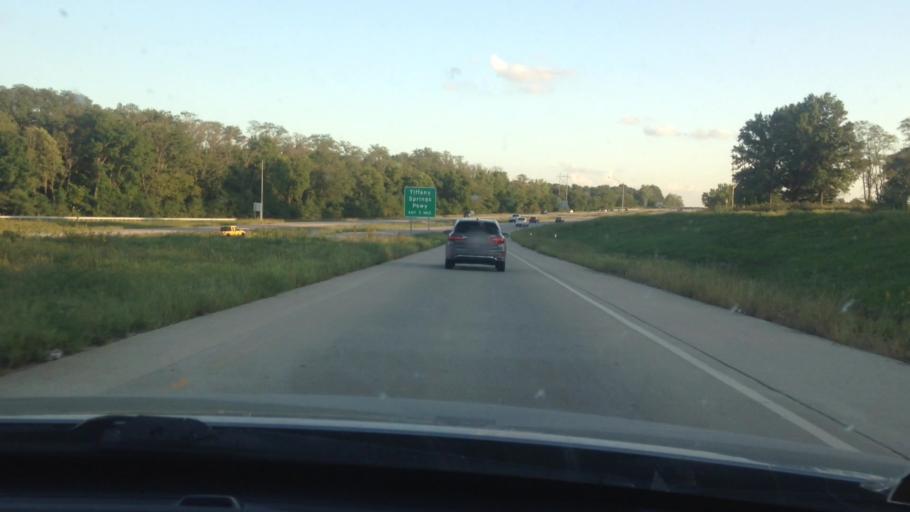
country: US
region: Missouri
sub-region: Clay County
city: Gladstone
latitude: 39.2885
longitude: -94.5861
